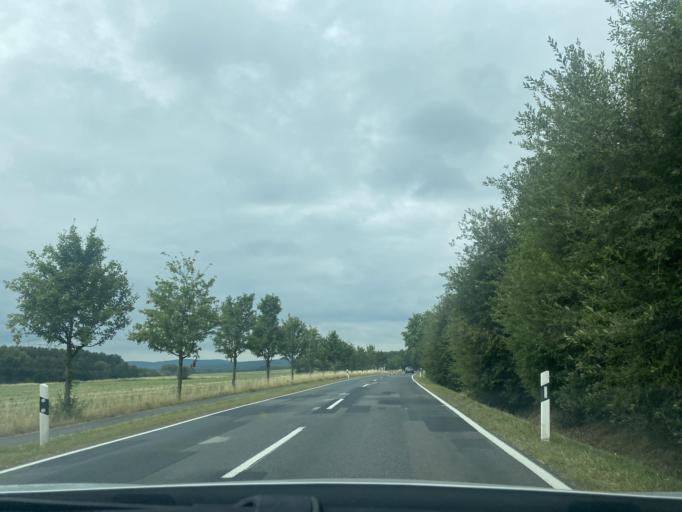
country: DE
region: Saxony
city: Quitzdorf
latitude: 51.2914
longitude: 14.7732
